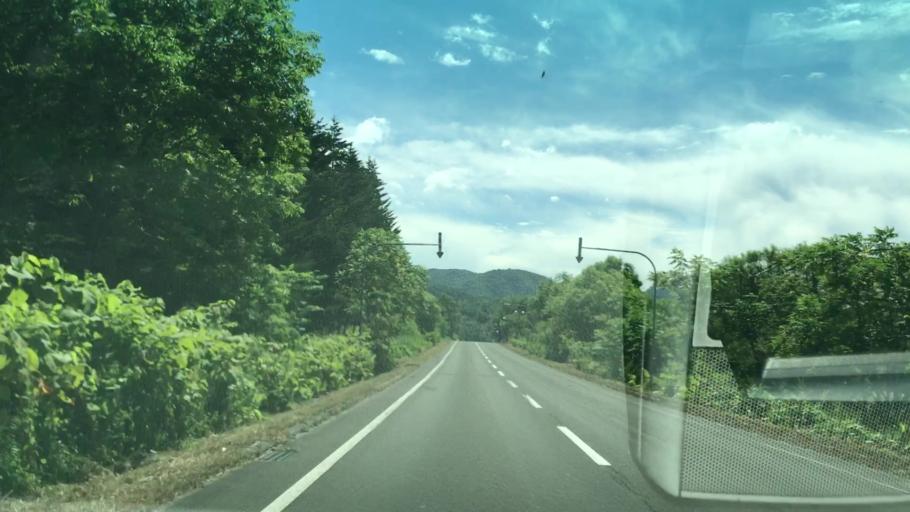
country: JP
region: Hokkaido
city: Shimo-furano
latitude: 42.9546
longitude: 142.4325
